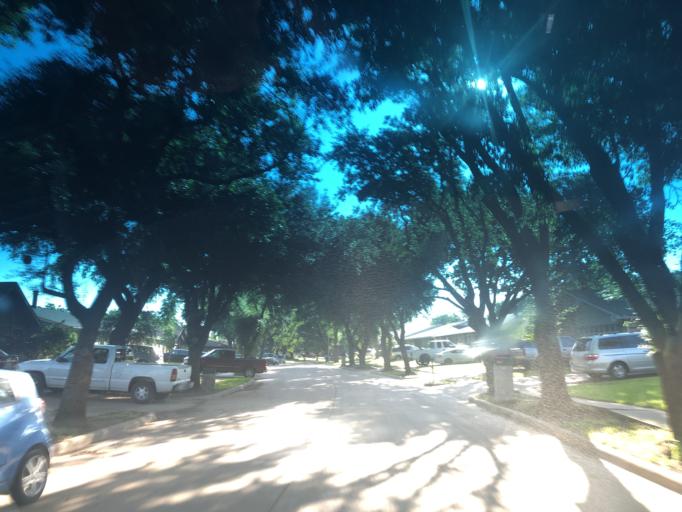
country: US
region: Texas
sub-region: Dallas County
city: Grand Prairie
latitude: 32.7027
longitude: -97.0014
